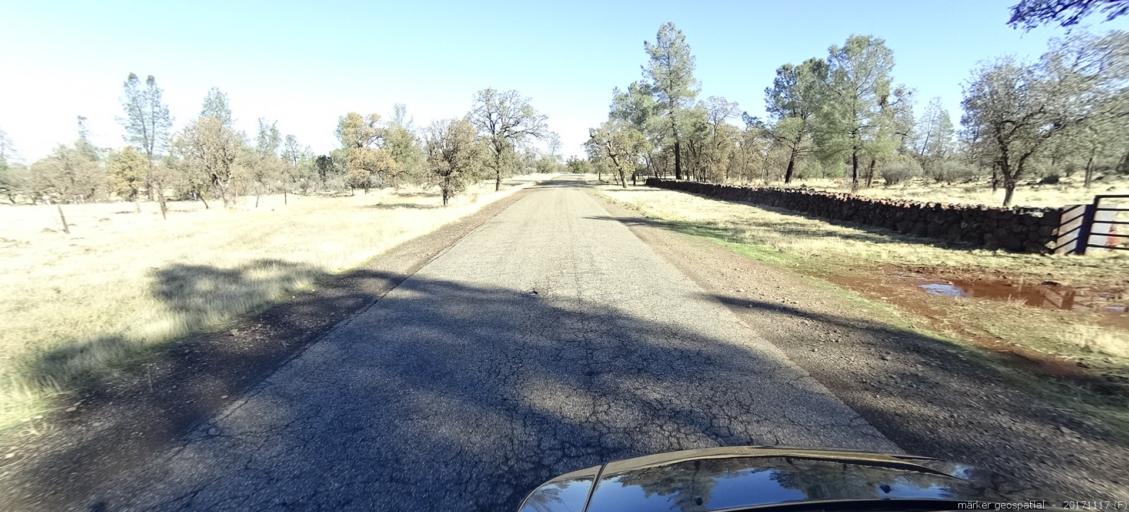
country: US
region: California
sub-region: Shasta County
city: Palo Cedro
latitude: 40.4502
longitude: -122.1116
